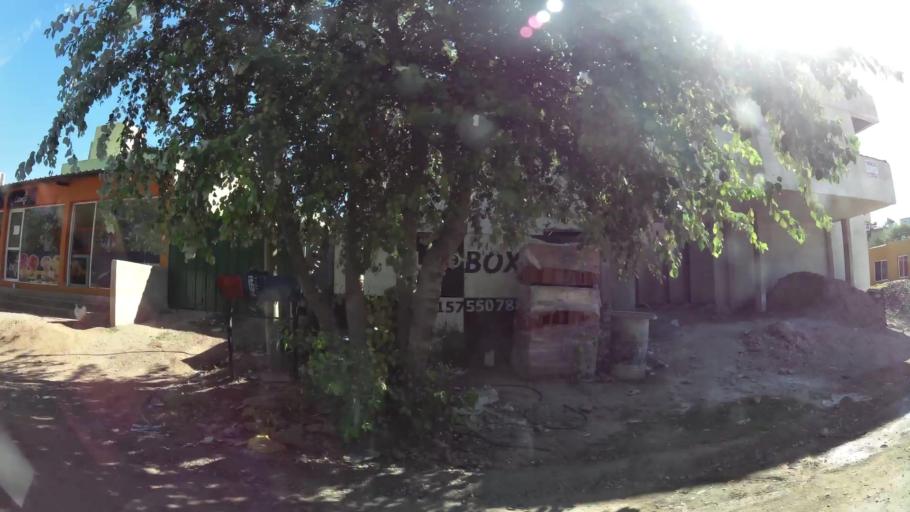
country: AR
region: Cordoba
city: La Calera
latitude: -31.3539
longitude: -64.3141
